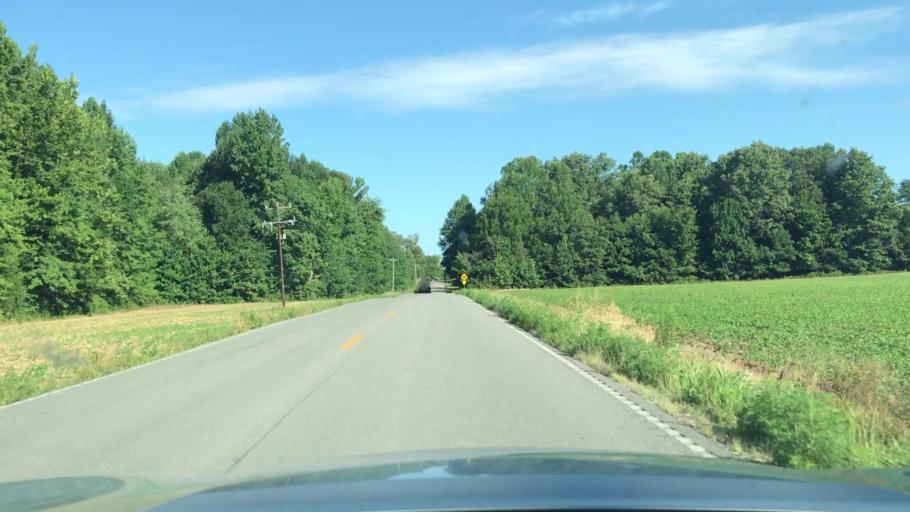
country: US
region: Kentucky
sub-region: Muhlenberg County
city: Greenville
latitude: 37.1291
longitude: -87.1375
